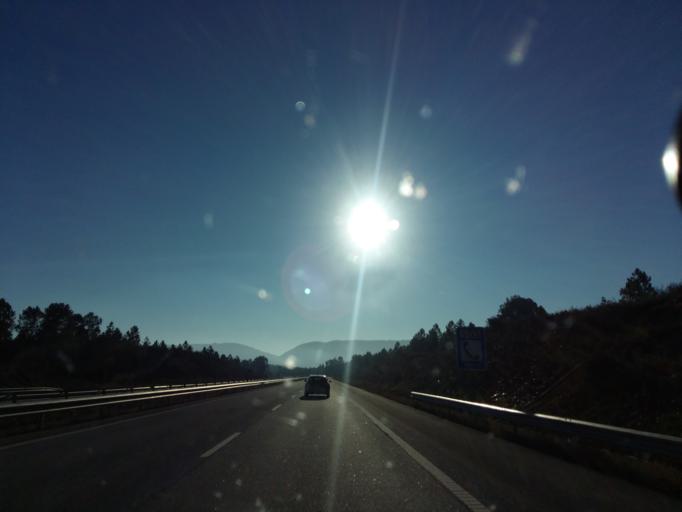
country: ES
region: Extremadura
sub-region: Provincia de Caceres
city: Cedillo
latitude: 39.7260
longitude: -7.6835
